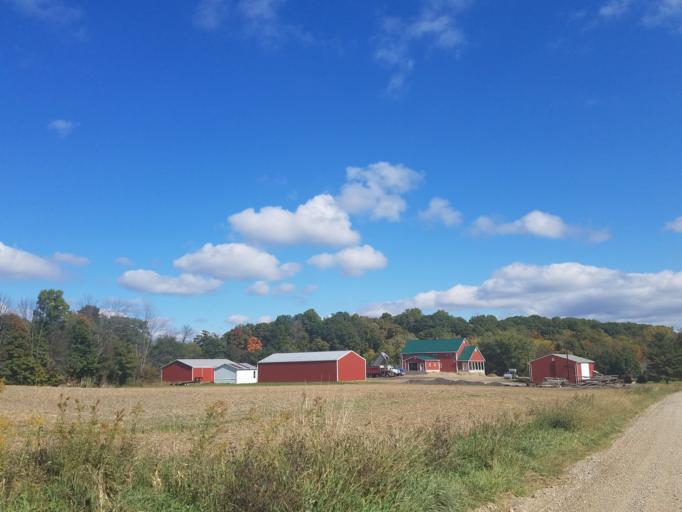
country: US
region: Ohio
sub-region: Richland County
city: Lexington
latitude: 40.5722
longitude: -82.6648
